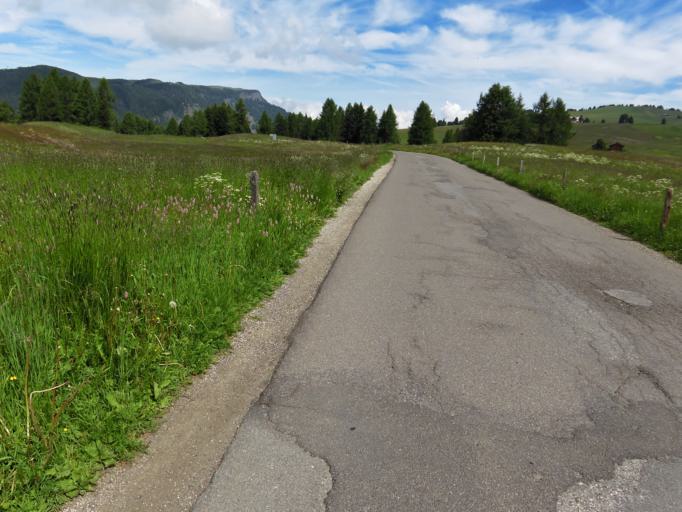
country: IT
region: Trentino-Alto Adige
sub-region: Bolzano
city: Ortisei
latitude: 46.5407
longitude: 11.6456
